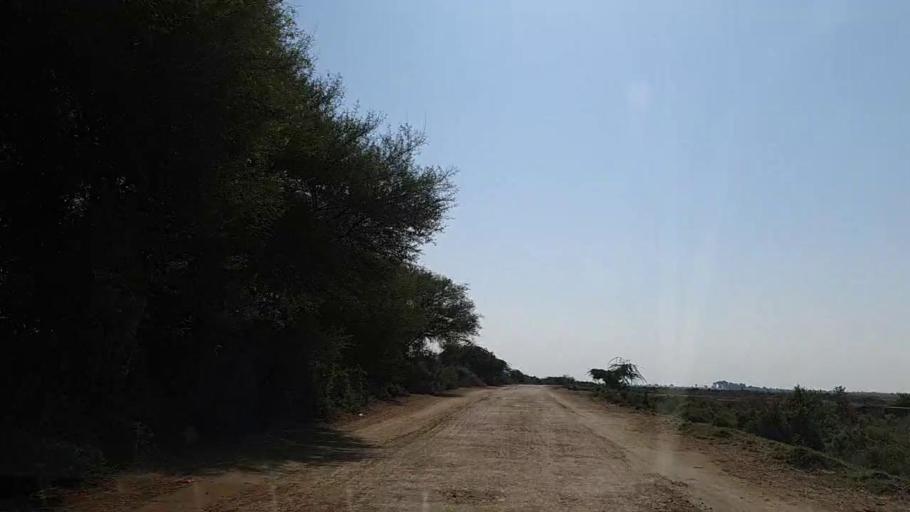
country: PK
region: Sindh
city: Chuhar Jamali
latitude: 24.5126
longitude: 68.0969
